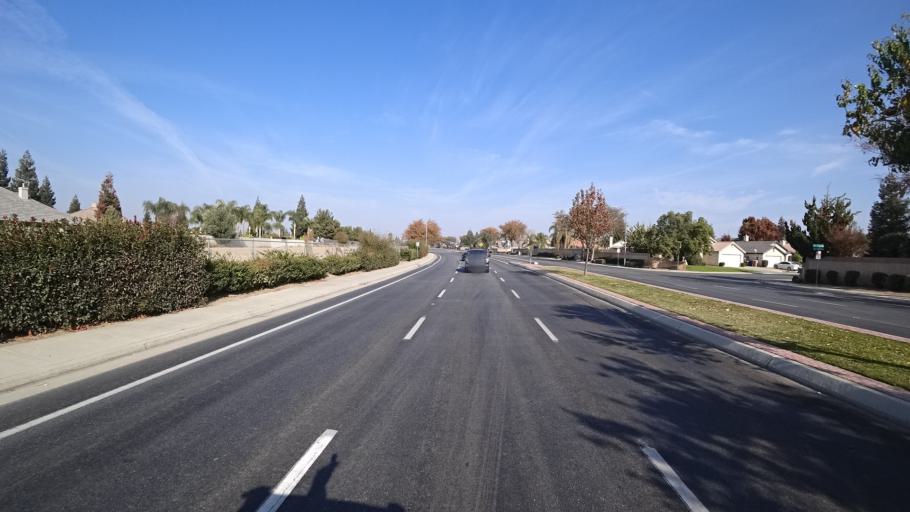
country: US
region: California
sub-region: Kern County
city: Greenacres
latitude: 35.3152
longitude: -119.1096
